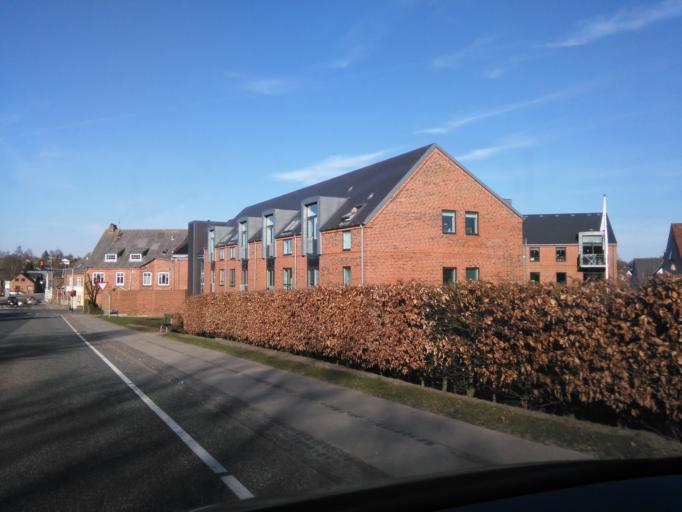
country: DK
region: Central Jutland
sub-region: Skanderborg Kommune
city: Ry
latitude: 55.9672
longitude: 9.7481
